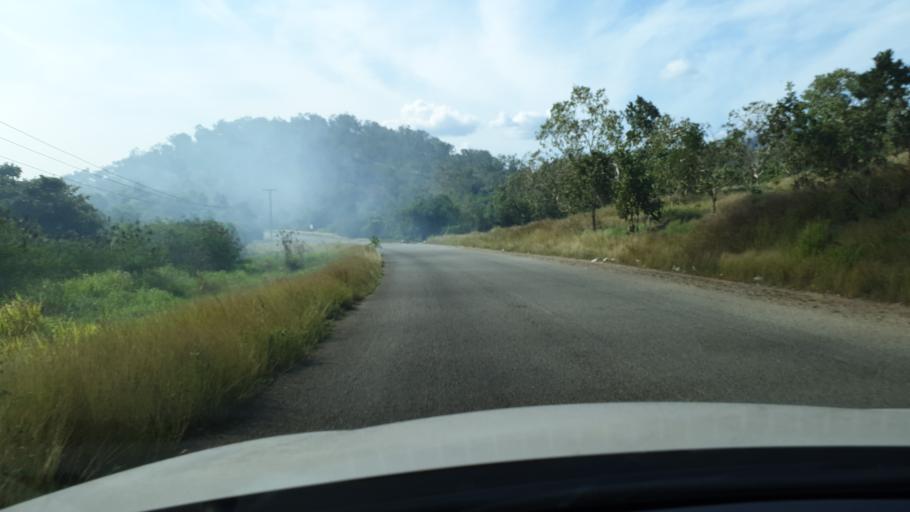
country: PG
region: National Capital
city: Port Moresby
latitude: -9.4995
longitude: 147.2965
